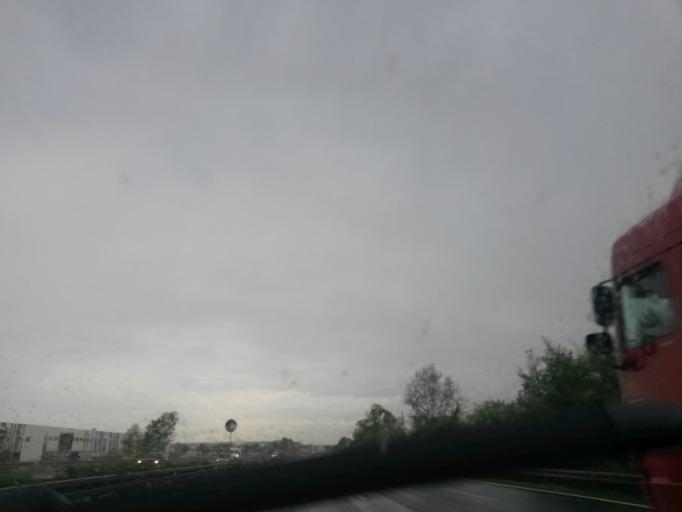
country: DE
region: Bavaria
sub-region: Upper Franconia
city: Forchheim
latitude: 49.6916
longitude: 11.0604
